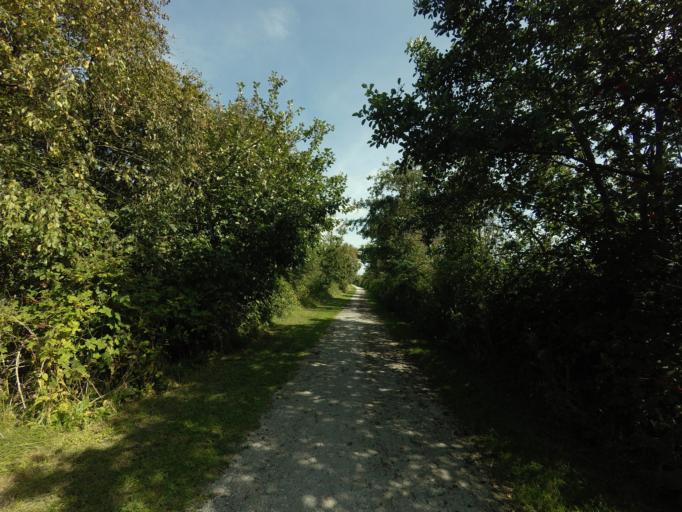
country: NL
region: Friesland
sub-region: Gemeente Ameland
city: Hollum
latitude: 53.4514
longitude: 5.6452
